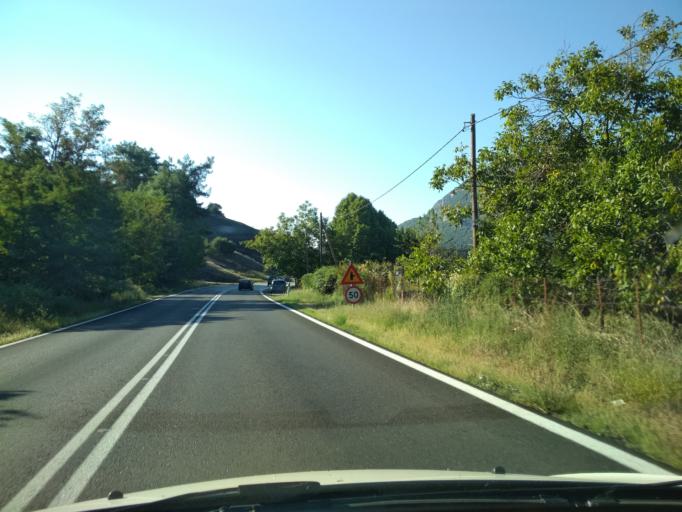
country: GR
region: Thessaly
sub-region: Trikala
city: Kastraki
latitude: 39.7060
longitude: 21.6114
